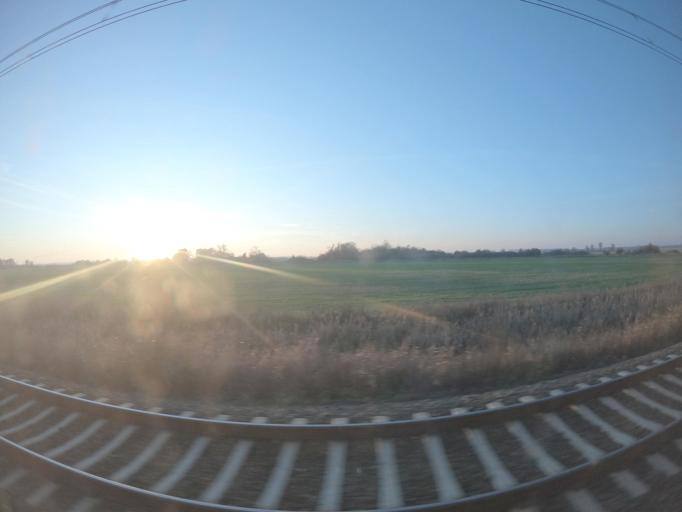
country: PL
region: Lubusz
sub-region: Powiat gorzowski
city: Kostrzyn nad Odra
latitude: 52.5427
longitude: 14.6509
